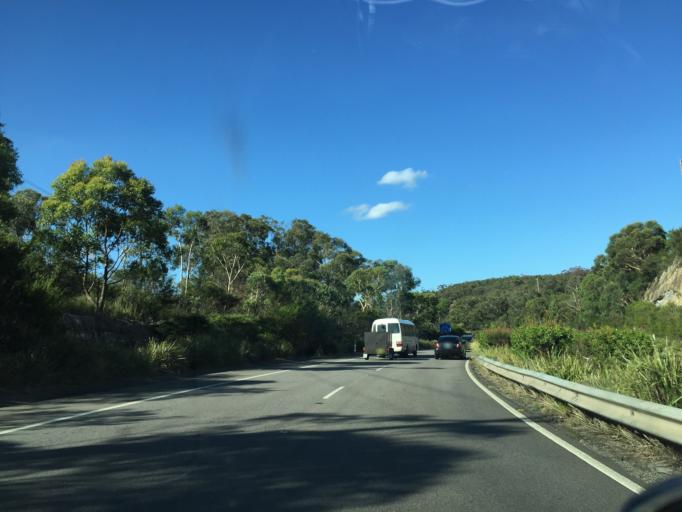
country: AU
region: New South Wales
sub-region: Blue Mountains Municipality
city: Hazelbrook
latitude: -33.7311
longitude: 150.4878
